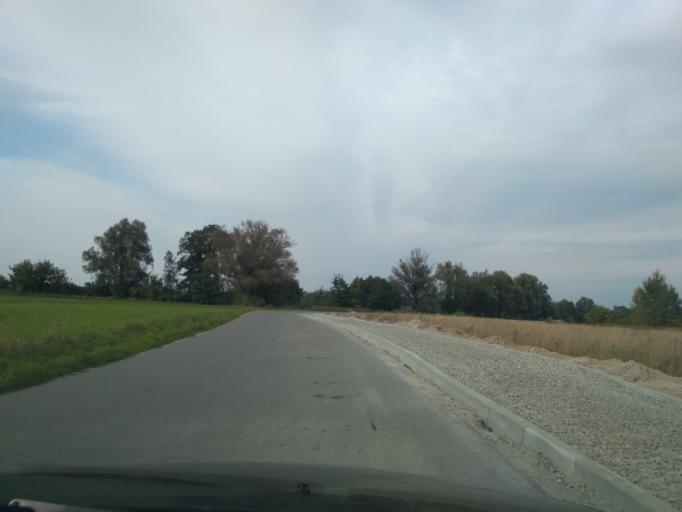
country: PL
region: Subcarpathian Voivodeship
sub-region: Powiat rzeszowski
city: Swilcza
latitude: 50.0840
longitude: 21.9137
